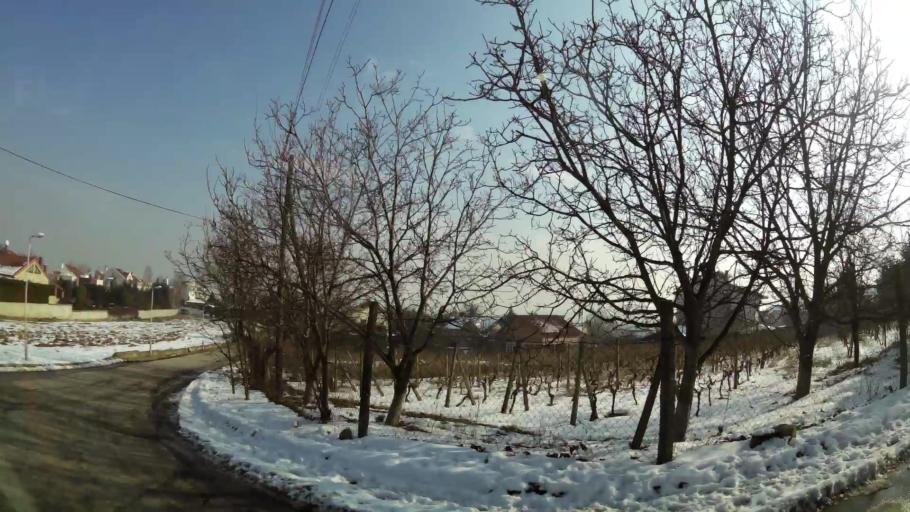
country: MK
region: Suto Orizari
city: Suto Orizare
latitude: 42.0296
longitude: 21.3789
